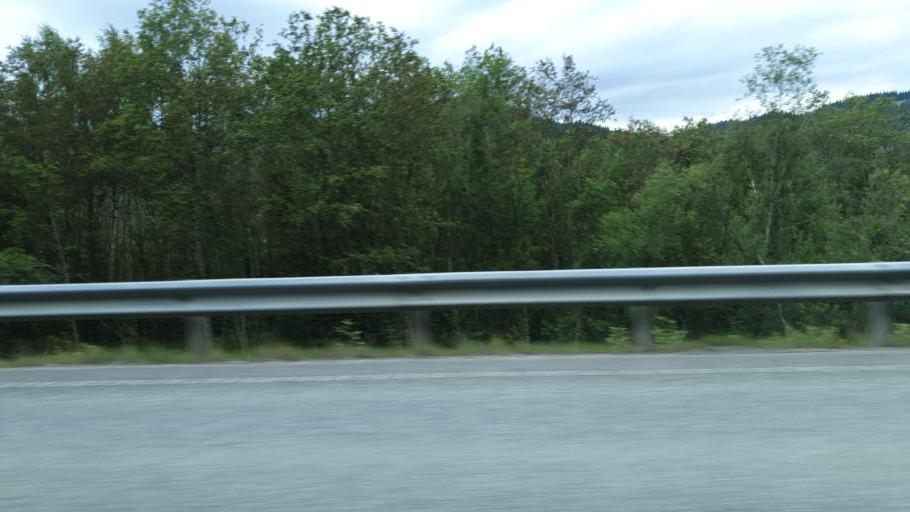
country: NO
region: Sor-Trondelag
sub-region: Midtre Gauldal
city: Storen
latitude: 63.0450
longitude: 10.2999
